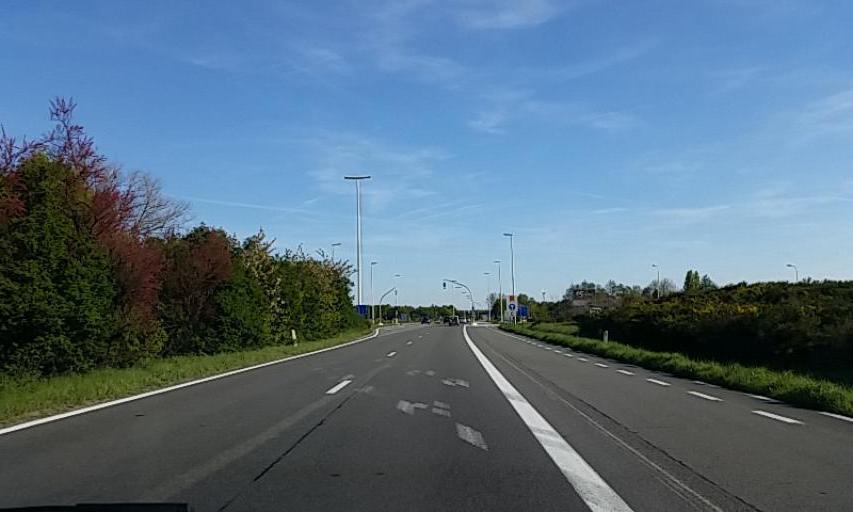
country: BE
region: Flanders
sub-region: Provincie Oost-Vlaanderen
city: Zelzate
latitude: 51.1992
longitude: 3.8271
